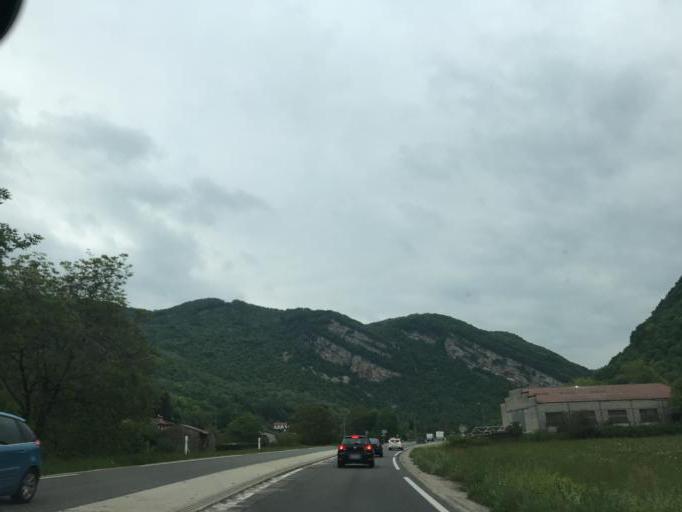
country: FR
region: Rhone-Alpes
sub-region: Departement de l'Ain
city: Saint-Rambert-en-Bugey
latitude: 45.9278
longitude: 5.4048
